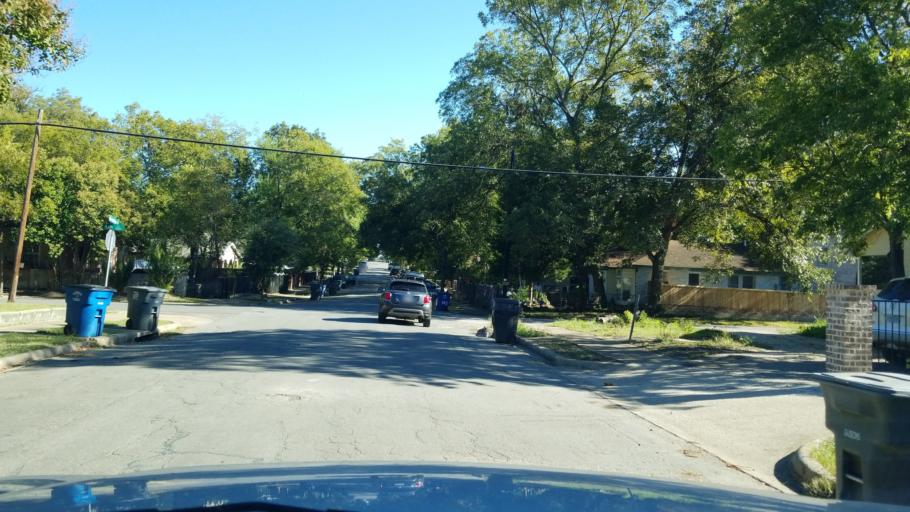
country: US
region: Texas
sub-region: Dallas County
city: Highland Park
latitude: 32.8003
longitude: -96.7502
